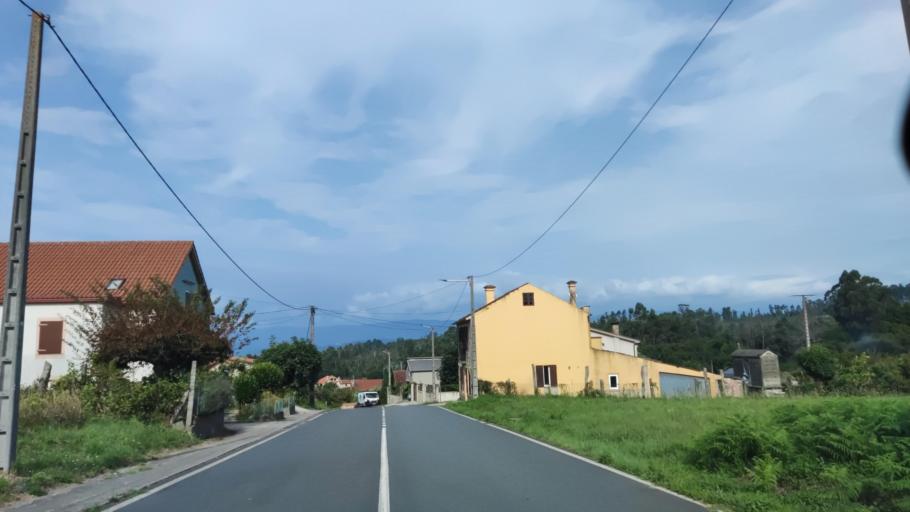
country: ES
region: Galicia
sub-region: Provincia da Coruna
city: Rianxo
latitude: 42.6476
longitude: -8.7921
